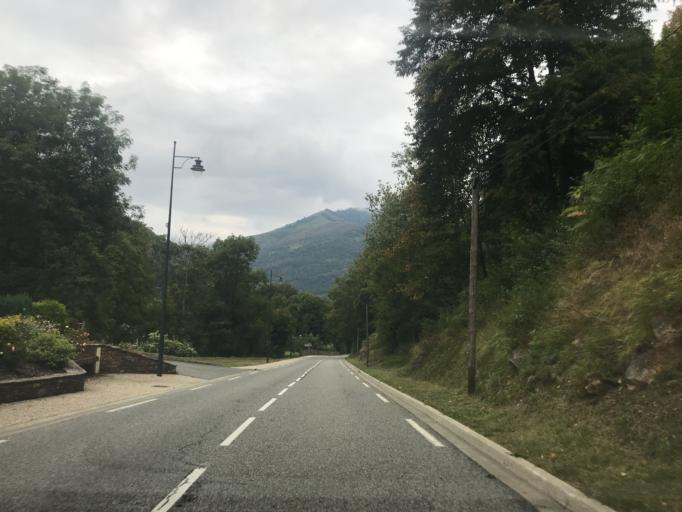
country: FR
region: Midi-Pyrenees
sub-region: Departement de la Haute-Garonne
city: Bagneres-de-Luchon
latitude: 42.7735
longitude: 0.6061
